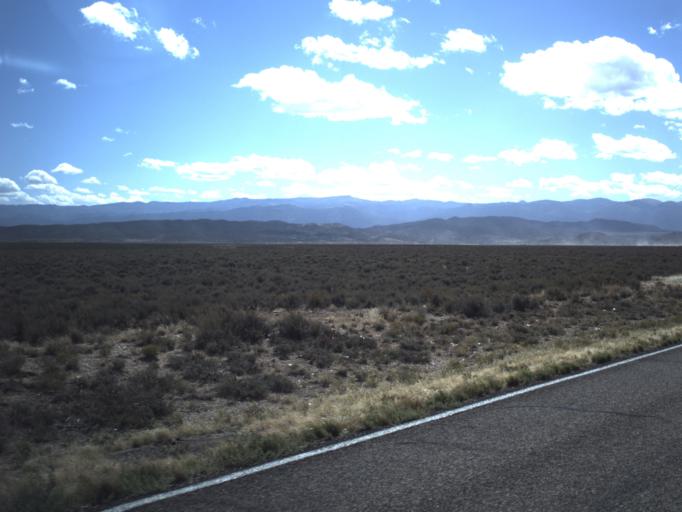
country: US
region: Utah
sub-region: Iron County
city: Enoch
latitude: 37.9811
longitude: -113.0033
